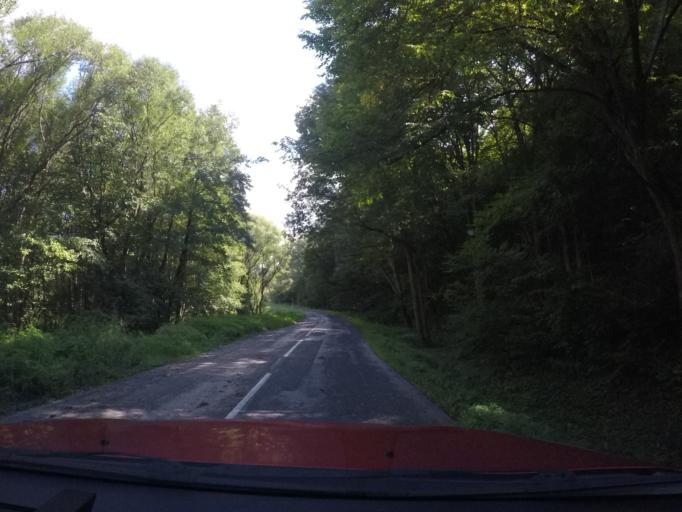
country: SK
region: Kosicky
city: Roznava
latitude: 48.6376
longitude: 20.6334
